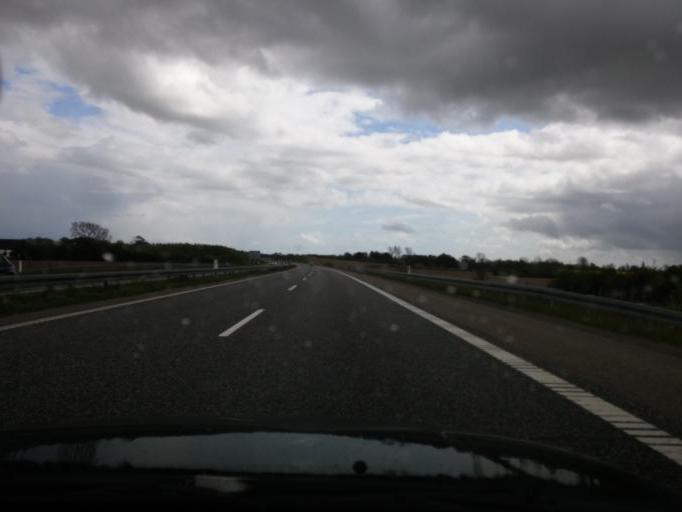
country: DK
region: South Denmark
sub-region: Faaborg-Midtfyn Kommune
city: Arslev
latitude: 55.2902
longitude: 10.4429
